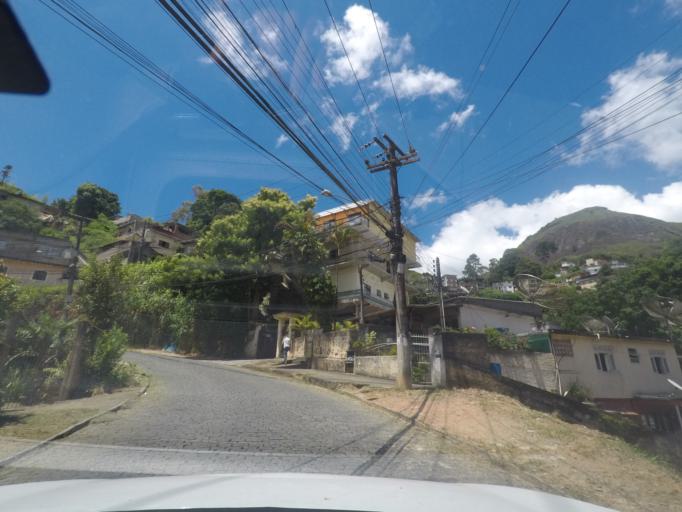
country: BR
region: Rio de Janeiro
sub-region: Teresopolis
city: Teresopolis
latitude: -22.4227
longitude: -42.9844
